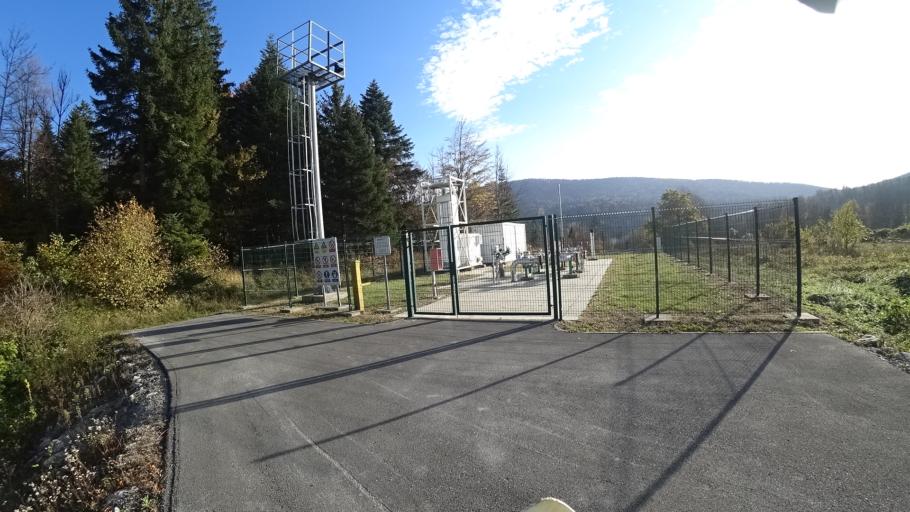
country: HR
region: Karlovacka
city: Plaski
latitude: 44.9762
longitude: 15.4006
